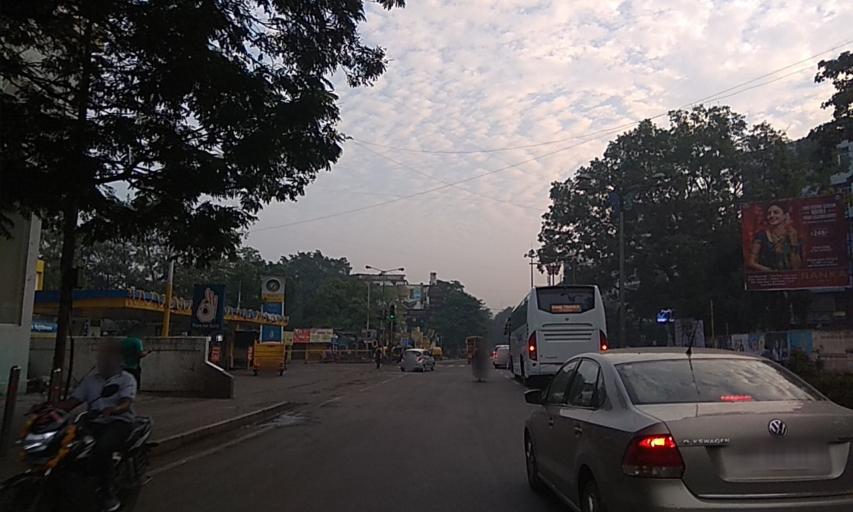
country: IN
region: Maharashtra
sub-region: Pune Division
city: Shivaji Nagar
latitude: 18.5342
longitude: 73.8792
